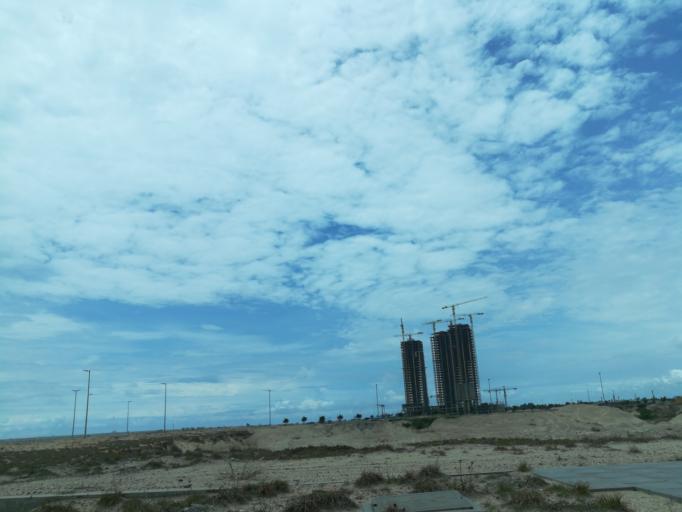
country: NG
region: Lagos
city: Ikoyi
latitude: 6.4040
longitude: 3.4143
